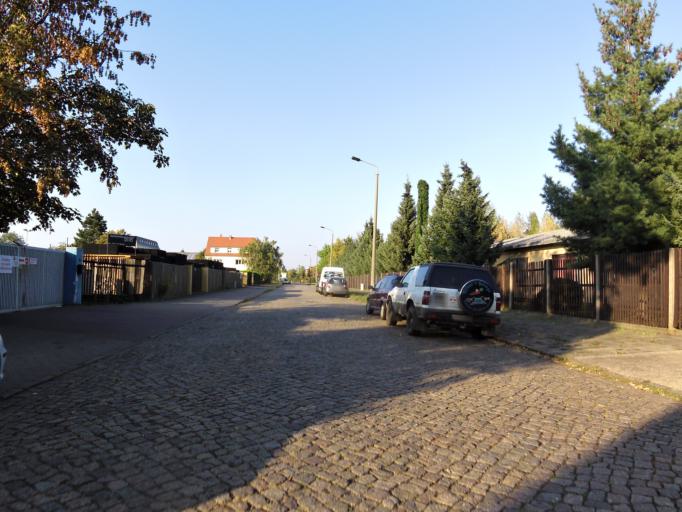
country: DE
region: Saxony
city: Leipzig
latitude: 51.3376
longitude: 12.3036
